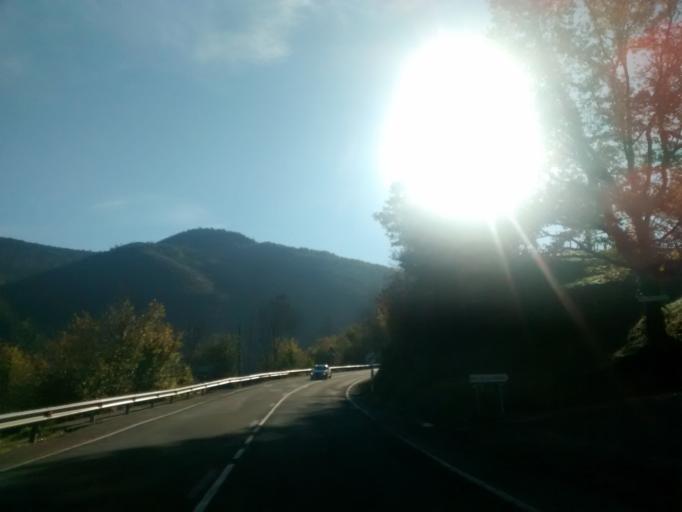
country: ES
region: Cantabria
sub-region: Provincia de Cantabria
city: Santiurde de Toranzo
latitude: 43.1615
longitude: -3.8977
